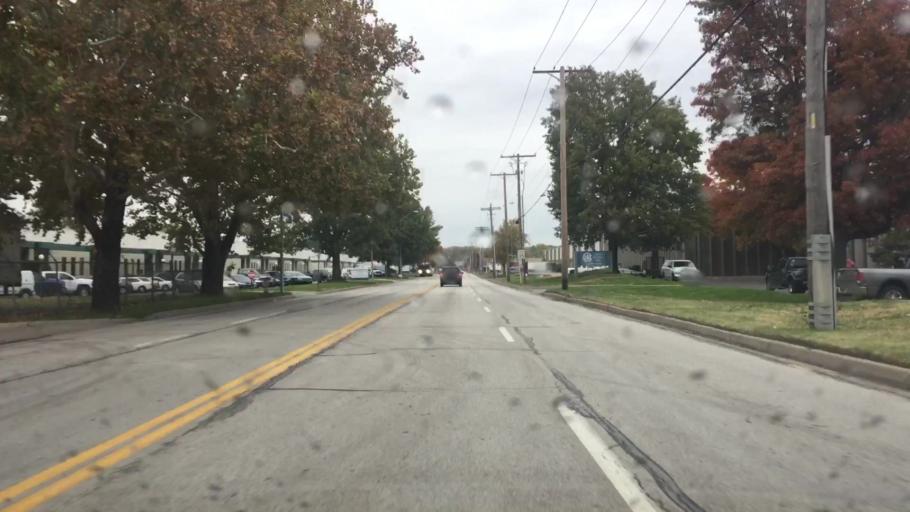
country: US
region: Missouri
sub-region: Clay County
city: North Kansas City
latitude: 39.1334
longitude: -94.5140
